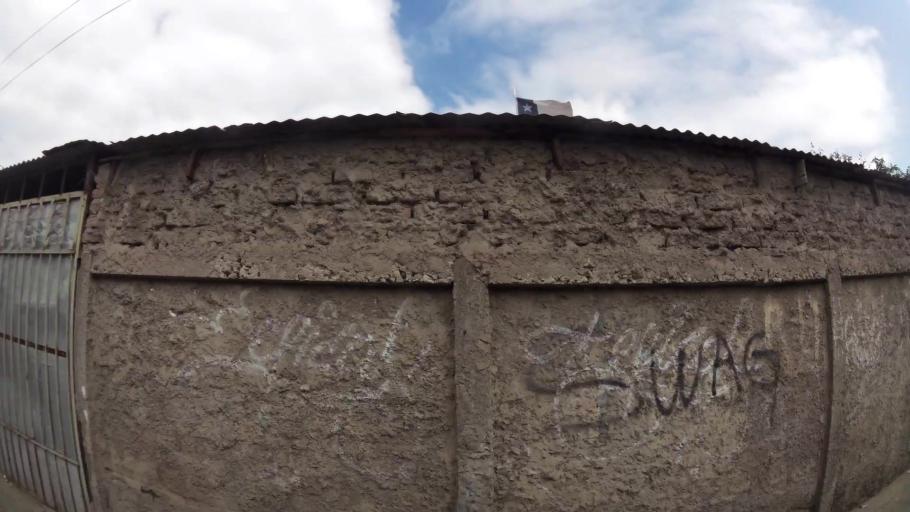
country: CL
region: Santiago Metropolitan
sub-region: Provincia de Maipo
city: San Bernardo
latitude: -33.5203
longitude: -70.7000
